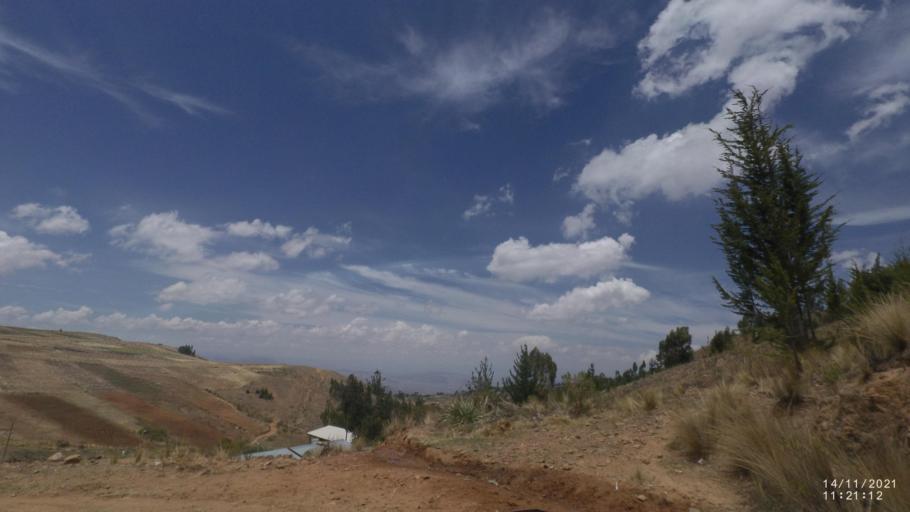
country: BO
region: Cochabamba
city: Cochabamba
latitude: -17.3364
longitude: -66.0367
